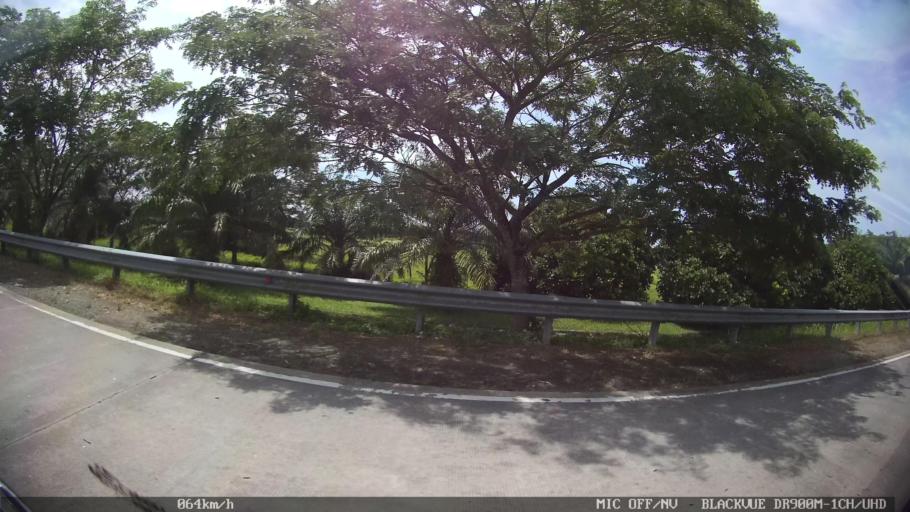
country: ID
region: North Sumatra
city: Percut
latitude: 3.6294
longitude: 98.8746
